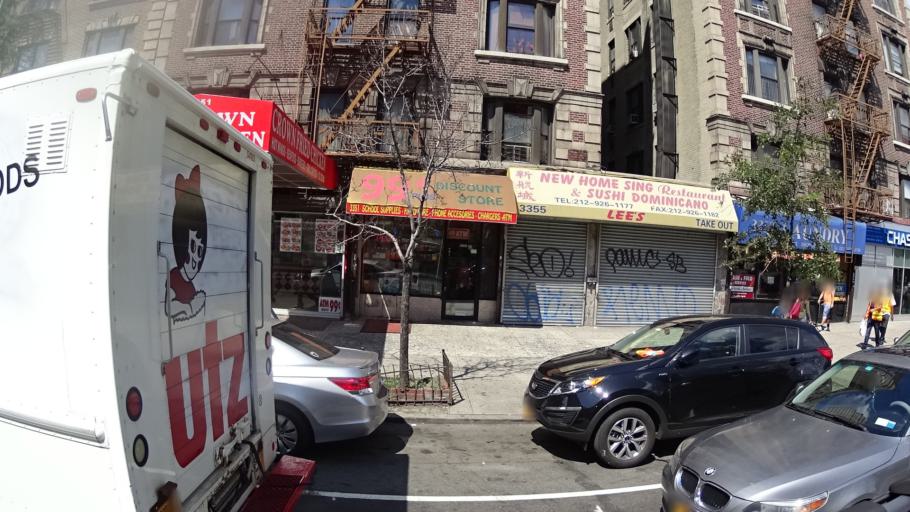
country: US
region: New Jersey
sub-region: Bergen County
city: Edgewater
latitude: 40.8205
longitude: -73.9549
